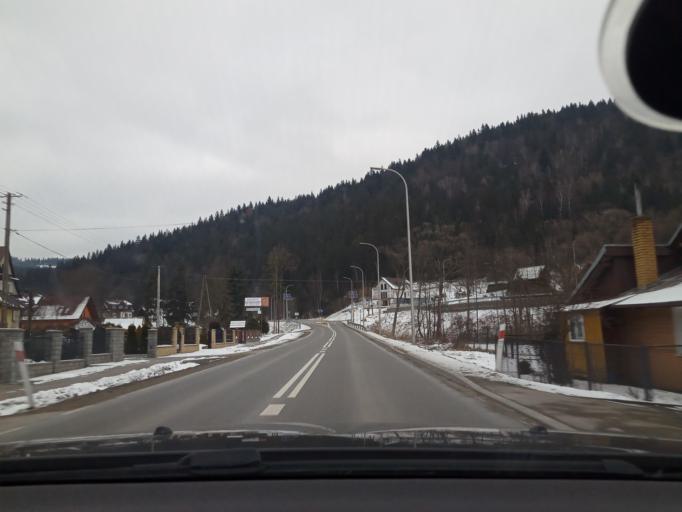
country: PL
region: Lesser Poland Voivodeship
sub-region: Powiat limanowski
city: Kamienica
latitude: 49.6096
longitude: 20.2947
